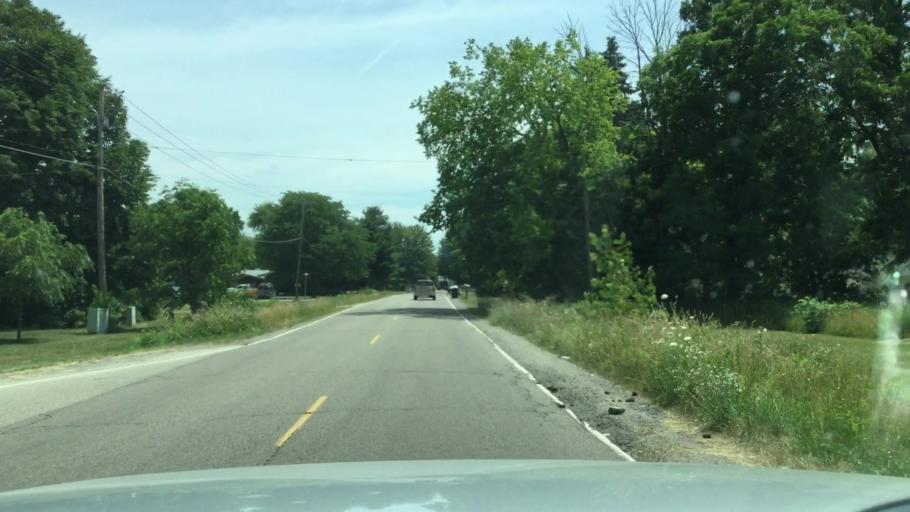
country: US
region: Michigan
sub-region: Genesee County
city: Swartz Creek
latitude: 43.0164
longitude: -83.7935
